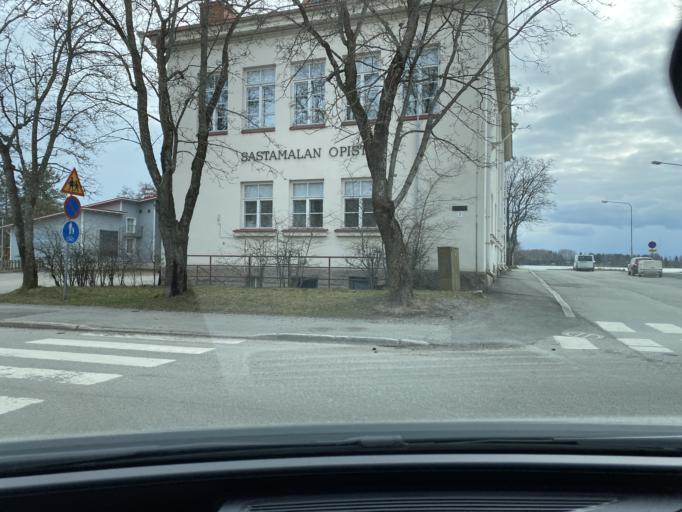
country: FI
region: Pirkanmaa
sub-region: Lounais-Pirkanmaa
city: Vammala
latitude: 61.3402
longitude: 22.9073
